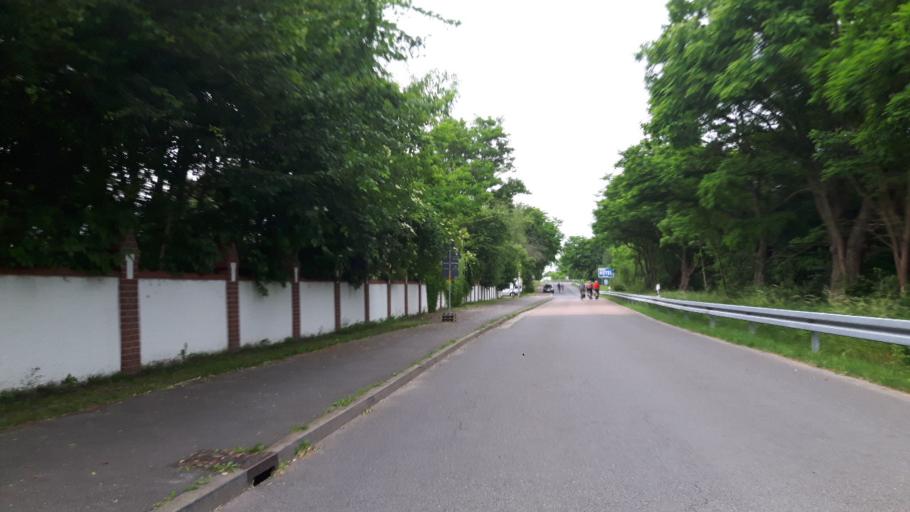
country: DE
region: Saxony-Anhalt
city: Wittenburg
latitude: 51.8539
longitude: 12.6456
